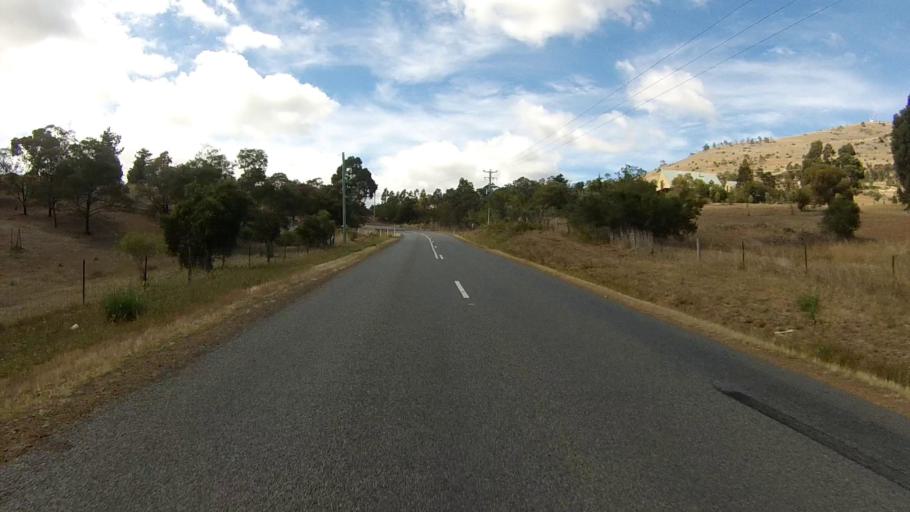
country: AU
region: Tasmania
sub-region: Glenorchy
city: Austins Ferry
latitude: -42.7256
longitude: 147.2845
